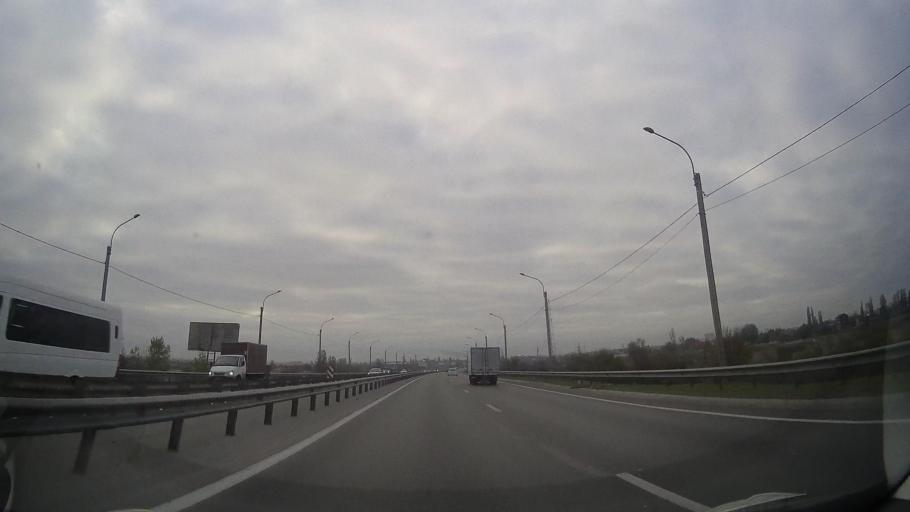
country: RU
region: Rostov
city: Bataysk
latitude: 47.1619
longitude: 39.7622
